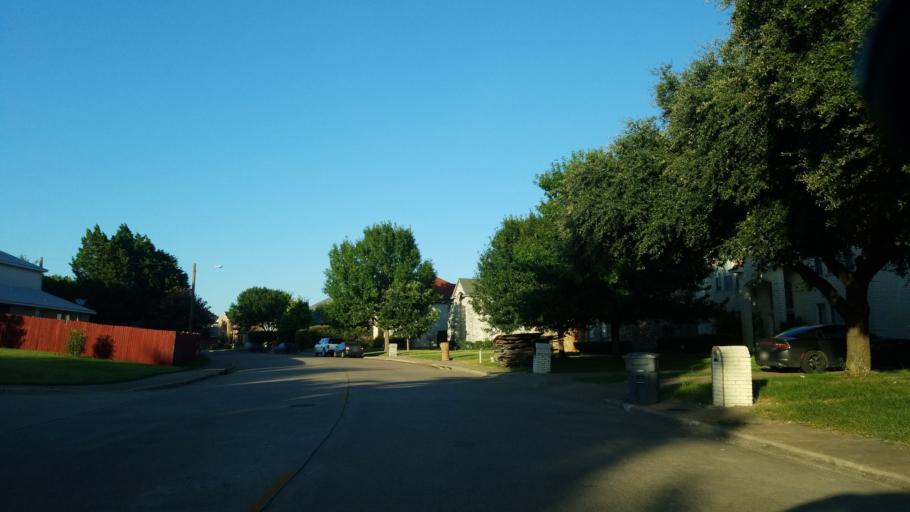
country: US
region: Texas
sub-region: Dallas County
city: Balch Springs
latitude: 32.7859
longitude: -96.6945
